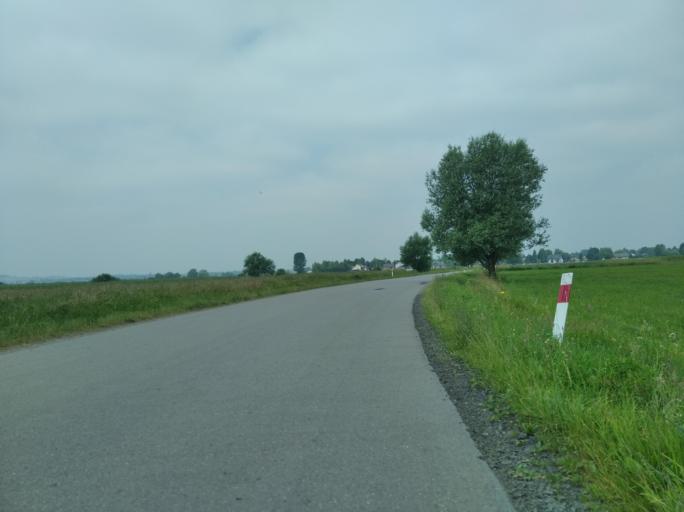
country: PL
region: Subcarpathian Voivodeship
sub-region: Powiat sanocki
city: Besko
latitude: 49.6124
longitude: 21.9515
